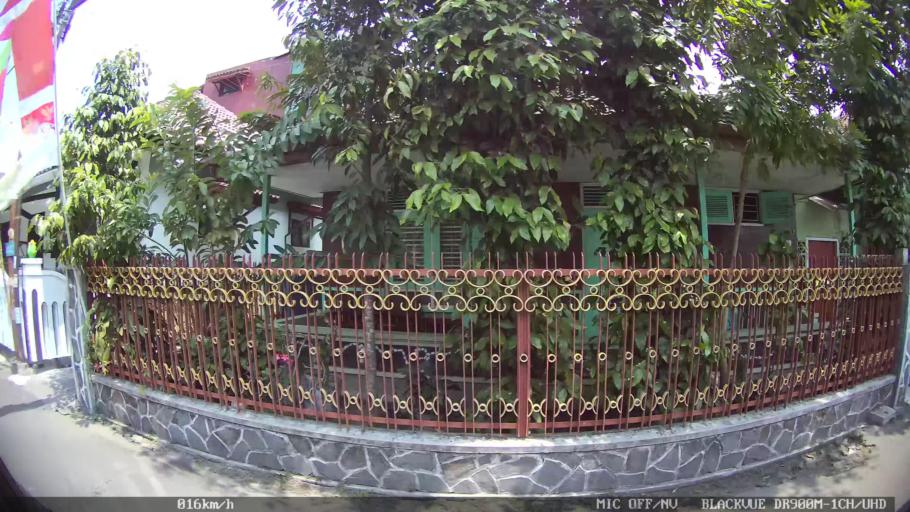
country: ID
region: Daerah Istimewa Yogyakarta
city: Yogyakarta
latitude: -7.8061
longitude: 110.4001
